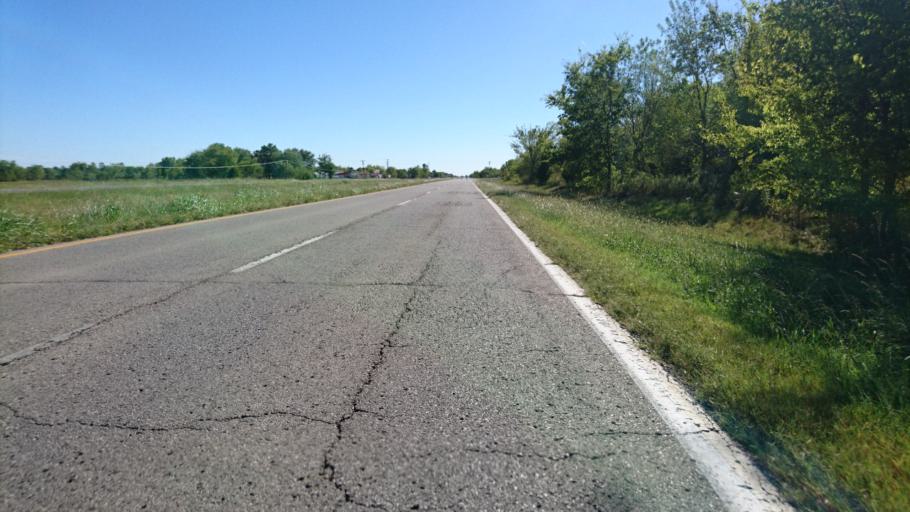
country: US
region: Oklahoma
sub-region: Rogers County
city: Bushyhead
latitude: 36.3975
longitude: -95.5474
